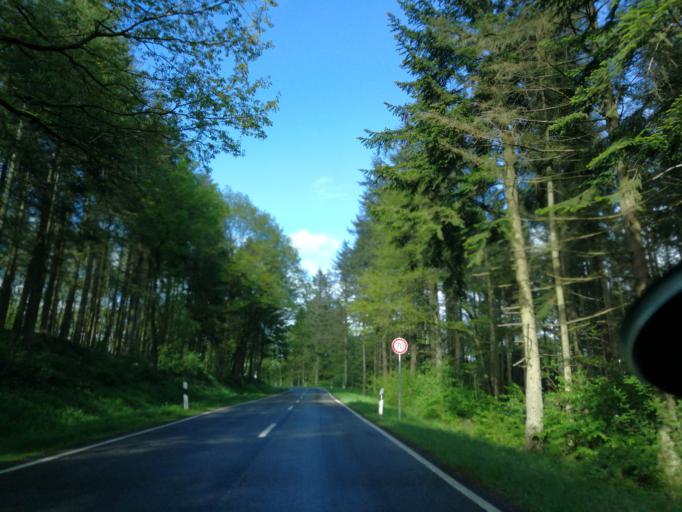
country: DE
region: Rheinland-Pfalz
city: Wittlich
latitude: 50.0085
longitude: 6.9005
